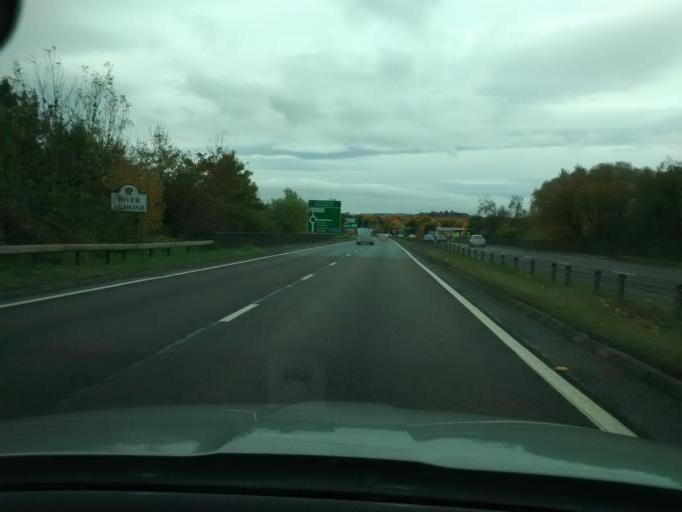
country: GB
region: Scotland
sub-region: Perth and Kinross
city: Luncarty
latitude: 56.4235
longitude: -3.4670
